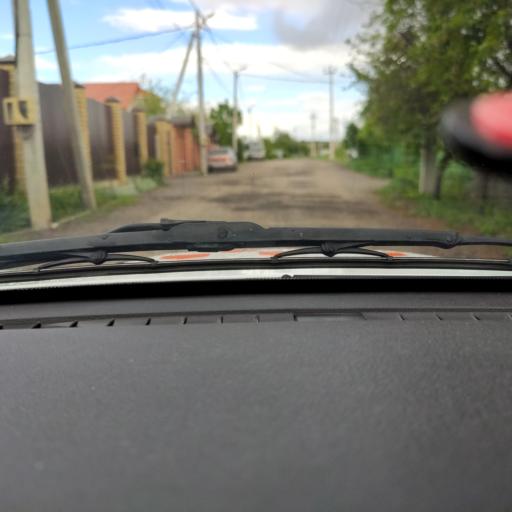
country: RU
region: Voronezj
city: Podgornoye
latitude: 51.7428
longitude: 39.1479
